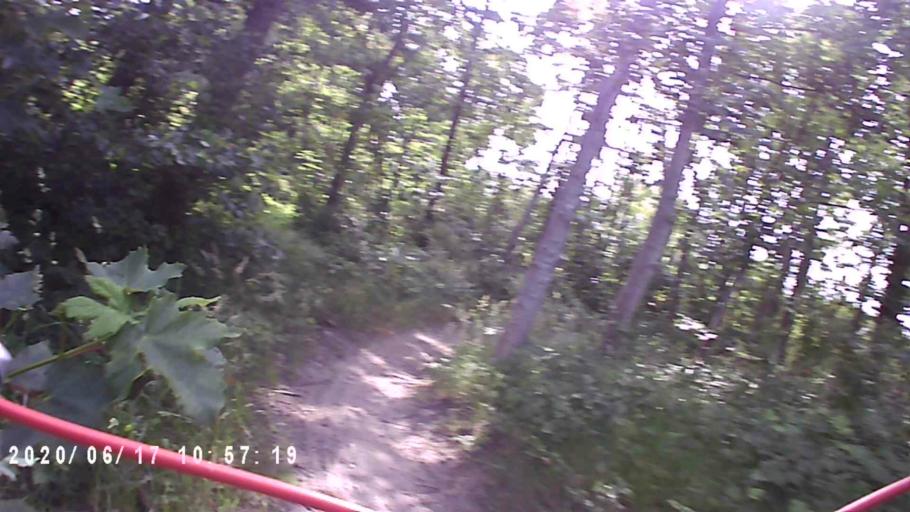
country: NL
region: Friesland
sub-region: Gemeente Dongeradeel
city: Anjum
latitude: 53.4061
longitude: 6.2081
